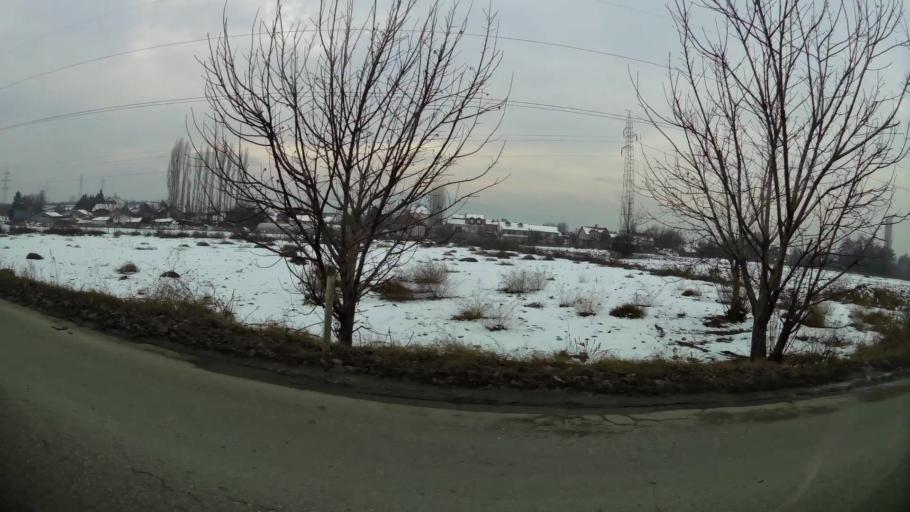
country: MK
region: Butel
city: Butel
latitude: 42.0401
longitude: 21.4538
